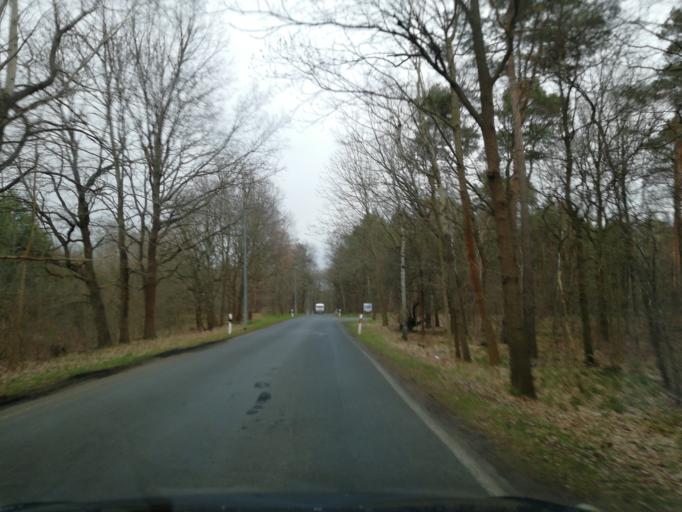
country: DE
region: Brandenburg
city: Calau
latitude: 51.7390
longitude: 13.9841
